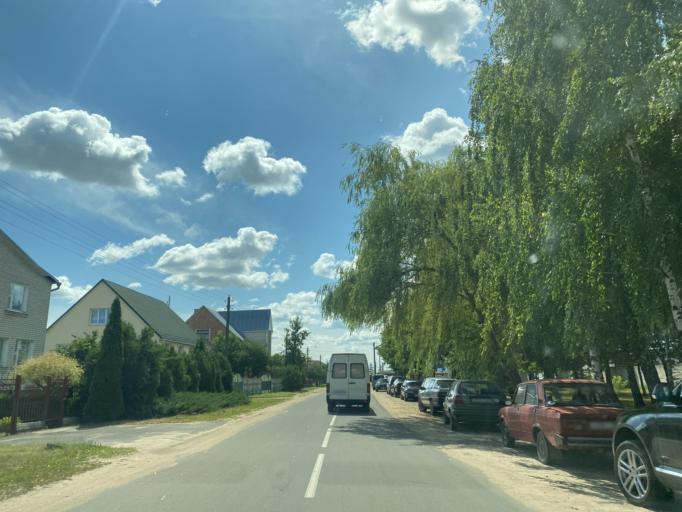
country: BY
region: Brest
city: Ivanava
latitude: 52.1456
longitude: 25.5465
